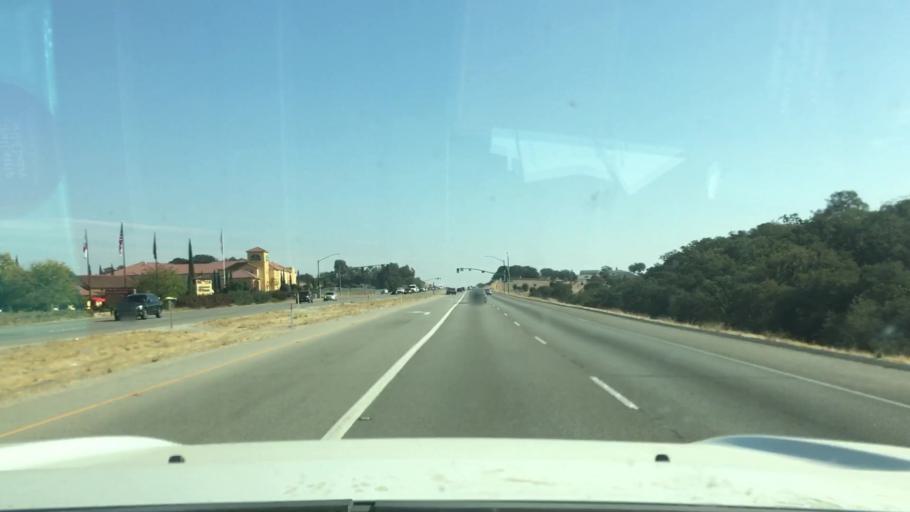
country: US
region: California
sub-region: San Luis Obispo County
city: Paso Robles
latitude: 35.6445
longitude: -120.6747
